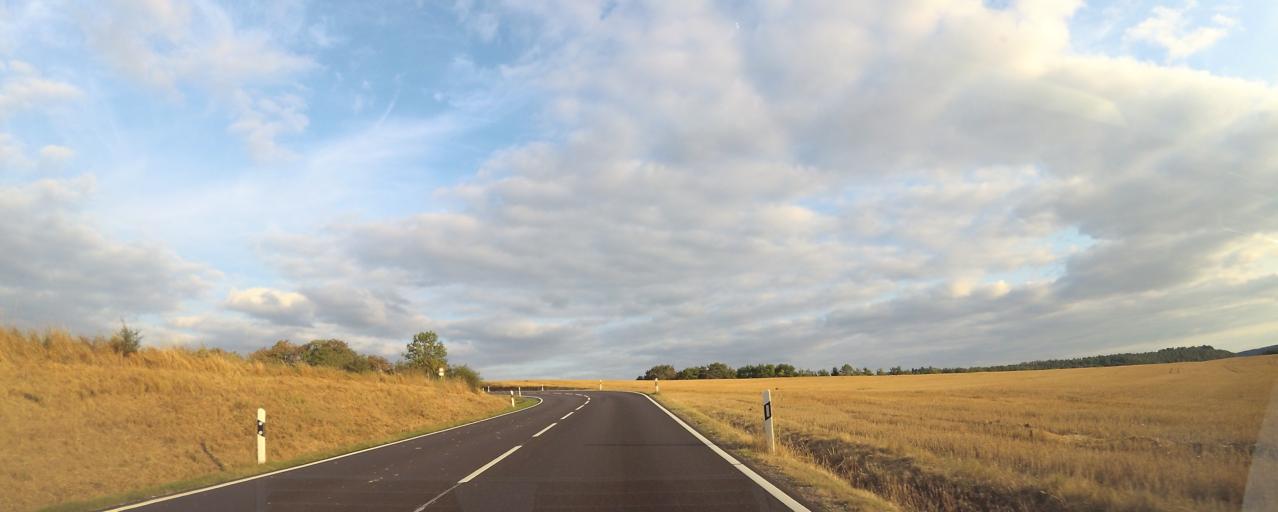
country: DE
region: Rheinland-Pfalz
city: Beilingen
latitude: 49.9656
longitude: 6.6515
